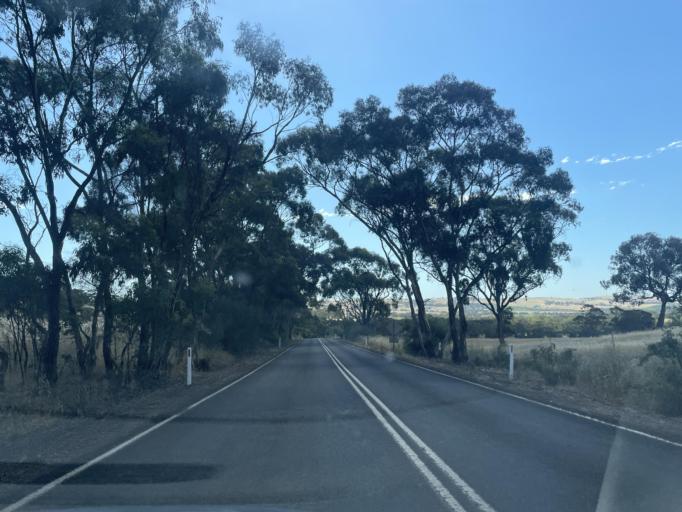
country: AU
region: South Australia
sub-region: Clare and Gilbert Valleys
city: Clare
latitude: -33.9049
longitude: 138.6979
